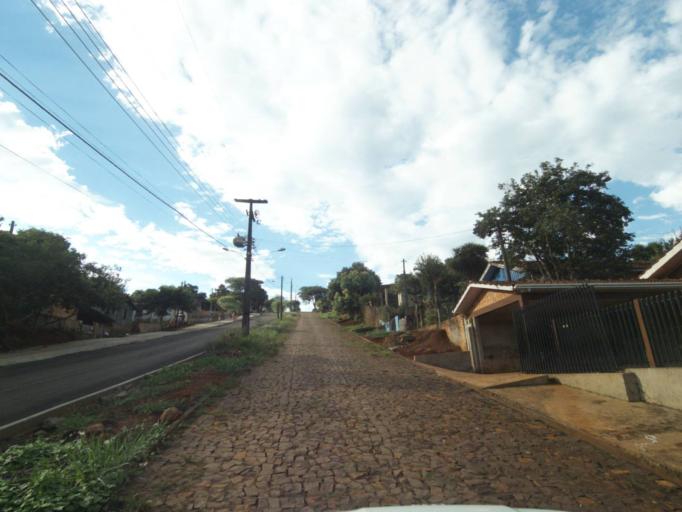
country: BR
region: Parana
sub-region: Laranjeiras Do Sul
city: Laranjeiras do Sul
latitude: -25.4921
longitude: -52.5240
